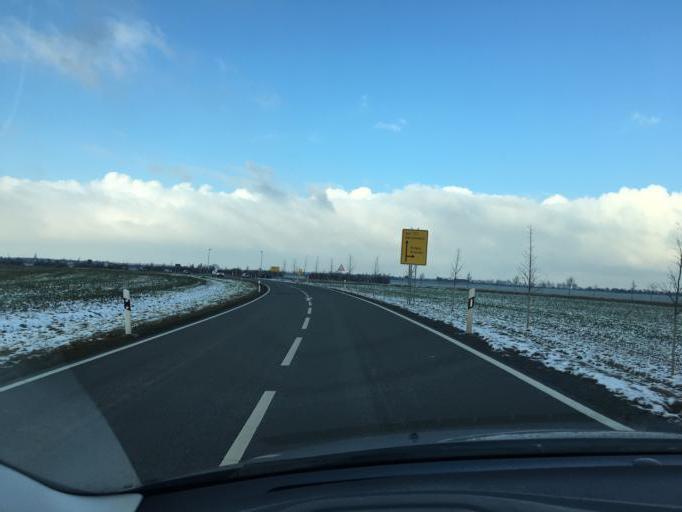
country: DE
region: Saxony
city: Brandis
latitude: 51.3423
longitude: 12.5973
